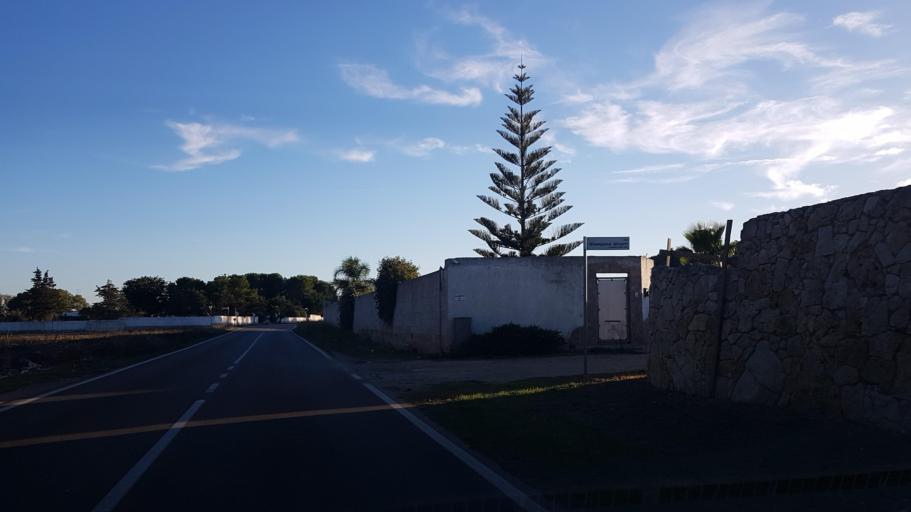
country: IT
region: Apulia
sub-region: Provincia di Lecce
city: Giorgilorio
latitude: 40.4005
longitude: 18.1963
